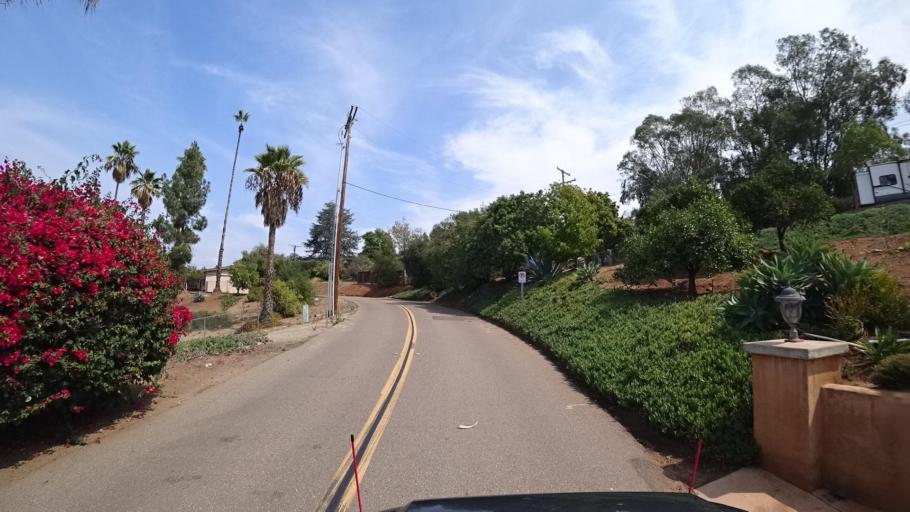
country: US
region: California
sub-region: San Diego County
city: Escondido
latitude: 33.0793
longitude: -117.0439
